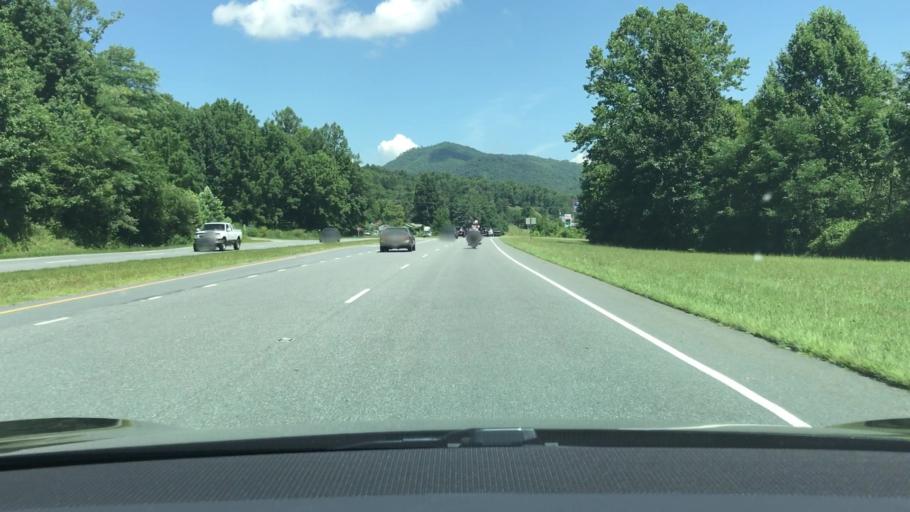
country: US
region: North Carolina
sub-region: Jackson County
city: Sylva
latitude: 35.3149
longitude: -83.2613
